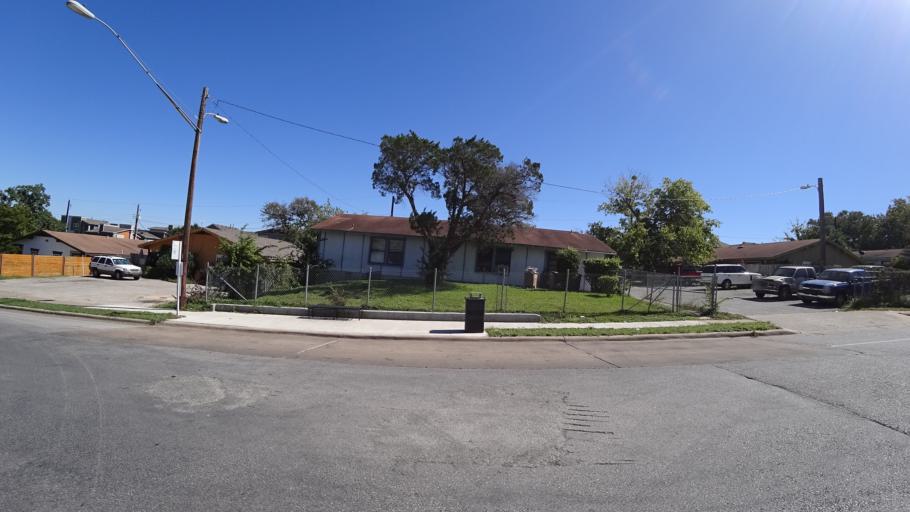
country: US
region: Texas
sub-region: Travis County
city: Austin
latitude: 30.2274
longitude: -97.7405
